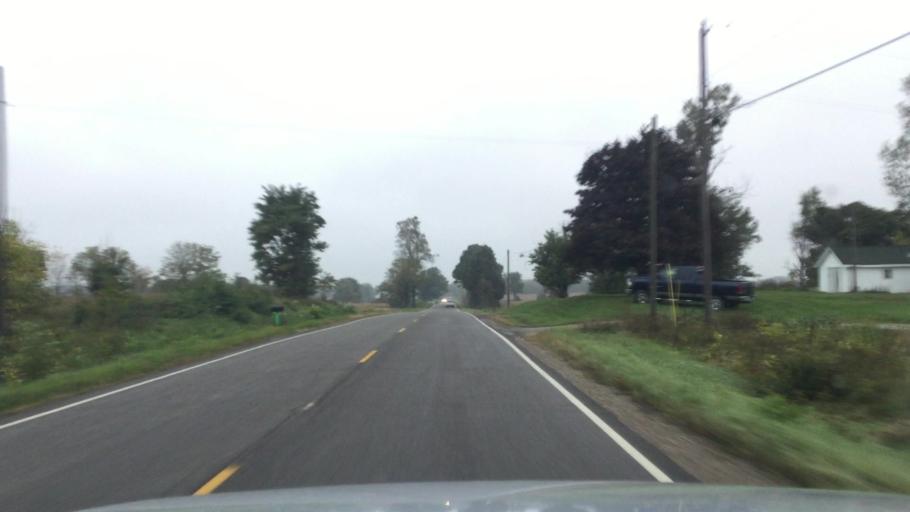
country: US
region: Michigan
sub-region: Shiawassee County
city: Corunna
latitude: 42.9182
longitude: -84.1240
